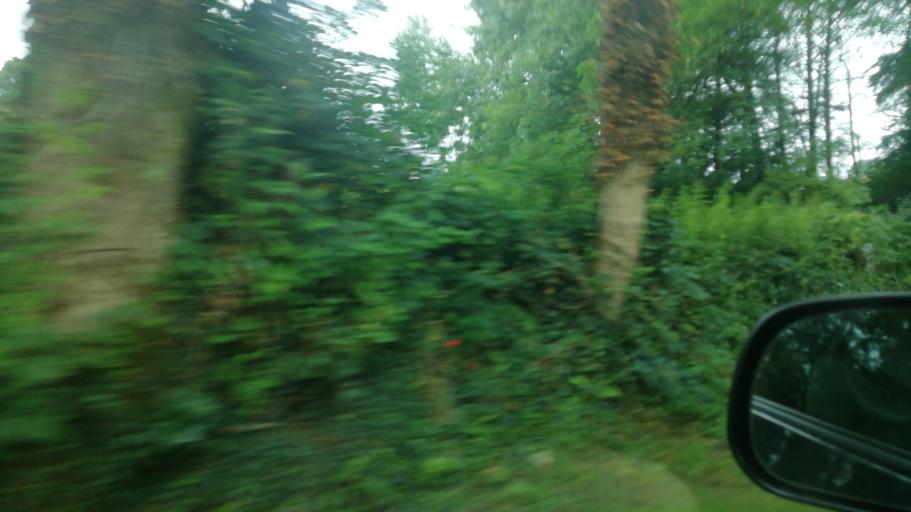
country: IE
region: Munster
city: Fethard
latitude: 52.5744
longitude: -7.5840
